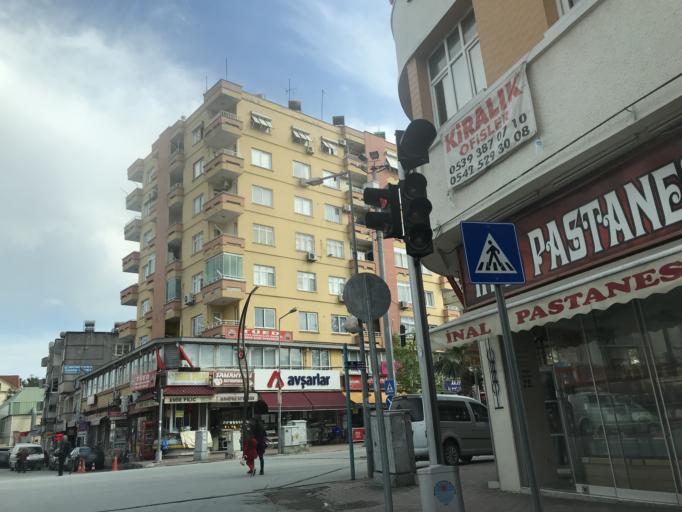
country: TR
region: Mersin
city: Tarsus
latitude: 36.9154
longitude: 34.8936
